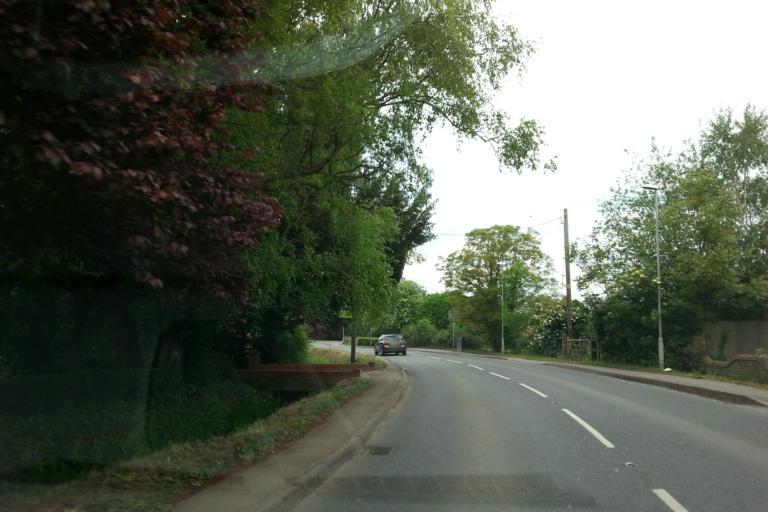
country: GB
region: England
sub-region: Cambridgeshire
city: Earith
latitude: 52.3045
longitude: 0.0528
